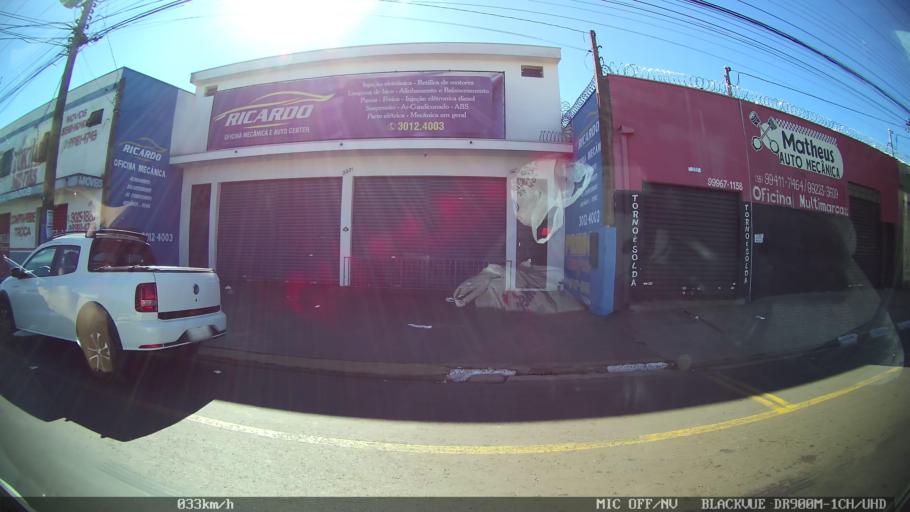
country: BR
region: Sao Paulo
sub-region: Franca
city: Franca
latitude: -20.5355
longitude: -47.3646
